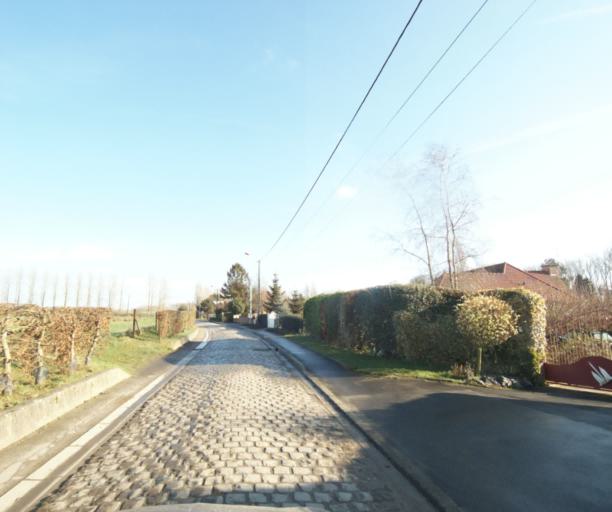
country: FR
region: Nord-Pas-de-Calais
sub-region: Departement du Nord
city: Preseau
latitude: 50.3123
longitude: 3.5812
